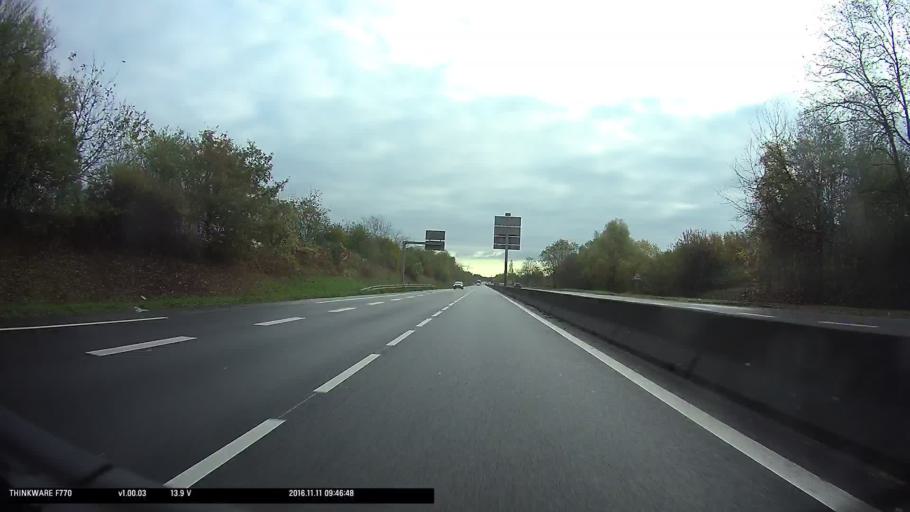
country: FR
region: Ile-de-France
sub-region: Departement du Val-d'Oise
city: Vaureal
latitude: 49.0581
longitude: 2.0348
